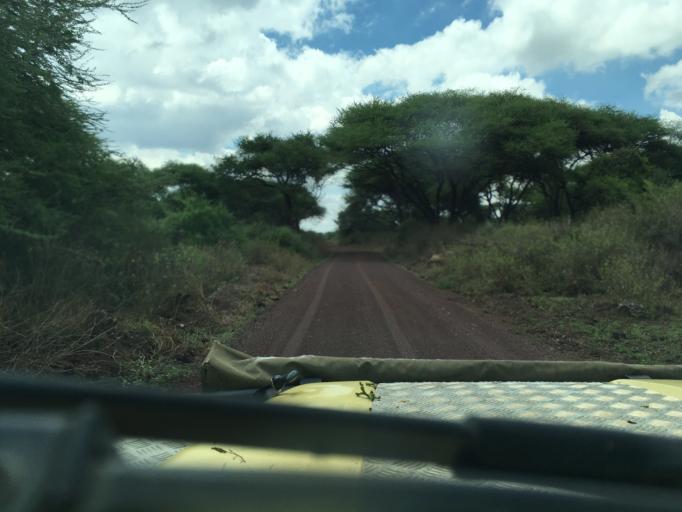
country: TZ
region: Arusha
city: Mto wa Mbu
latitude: -3.4253
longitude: 35.8147
